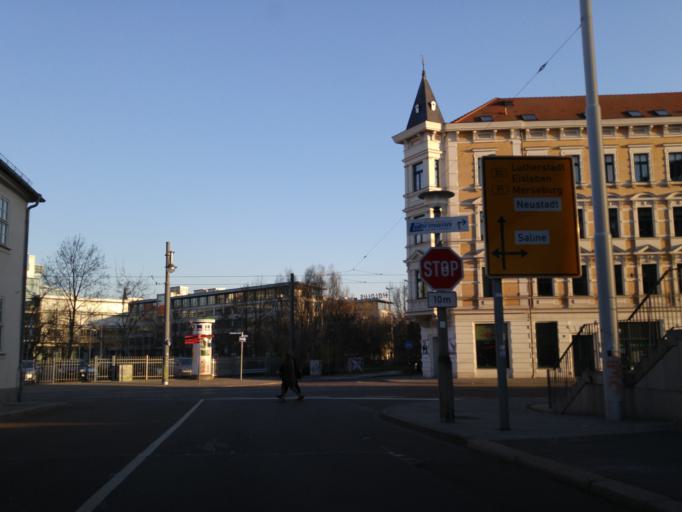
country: DE
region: Saxony-Anhalt
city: Halle (Saale)
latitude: 51.4822
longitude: 11.9622
